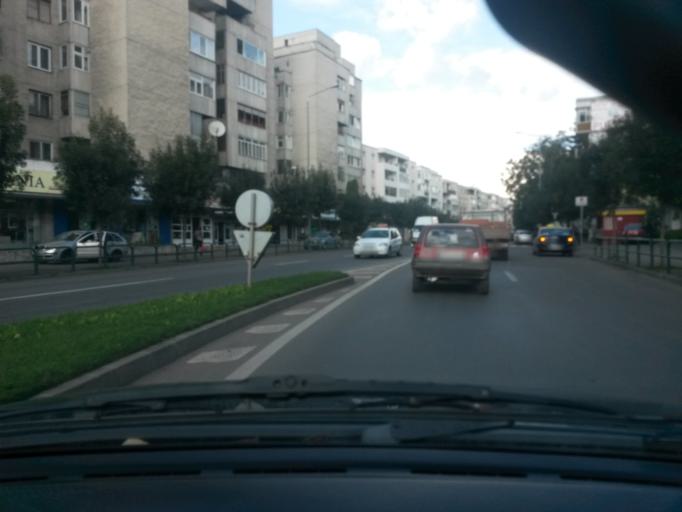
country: RO
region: Mures
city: Targu-Mures
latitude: 46.5541
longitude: 24.5694
